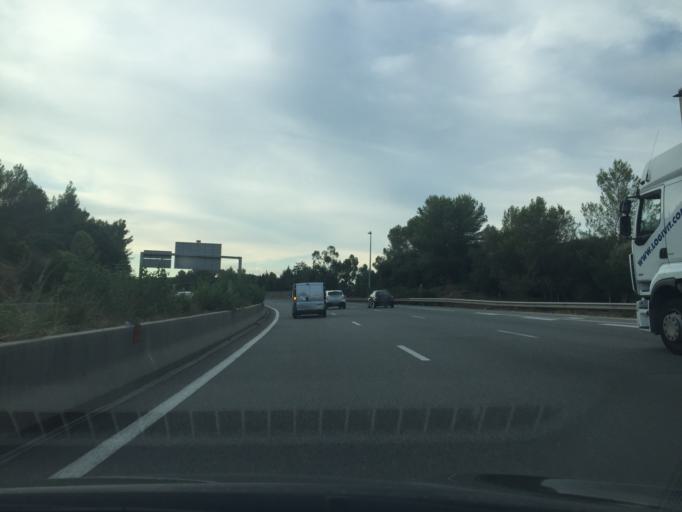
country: FR
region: Provence-Alpes-Cote d'Azur
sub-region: Departement du Var
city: Frejus
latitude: 43.4774
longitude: 6.7424
